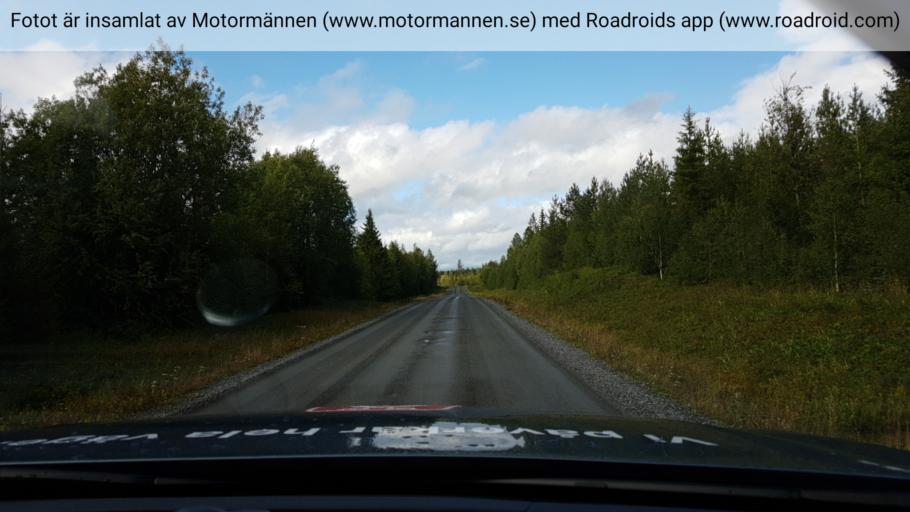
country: SE
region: Jaemtland
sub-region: Krokoms Kommun
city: Krokom
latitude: 63.7192
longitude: 14.5162
